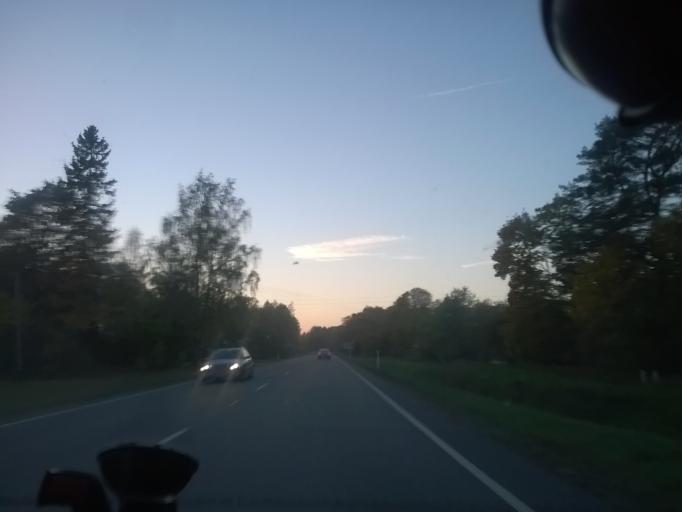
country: EE
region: Laeaene
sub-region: Ridala Parish
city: Uuemoisa
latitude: 58.9606
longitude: 23.7030
